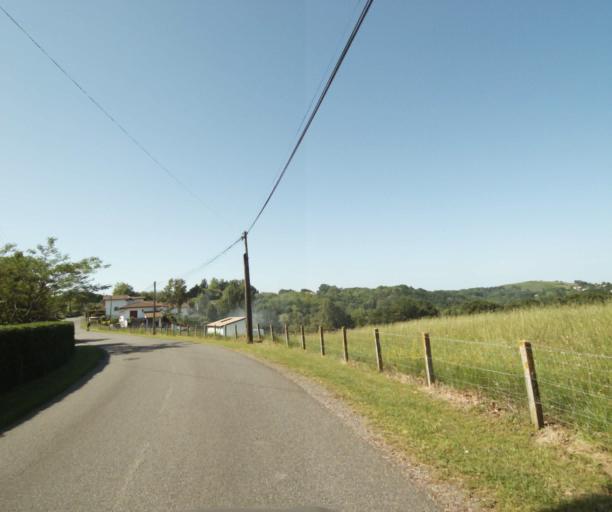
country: FR
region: Aquitaine
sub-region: Departement des Pyrenees-Atlantiques
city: Villefranque
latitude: 43.4616
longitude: -1.4487
